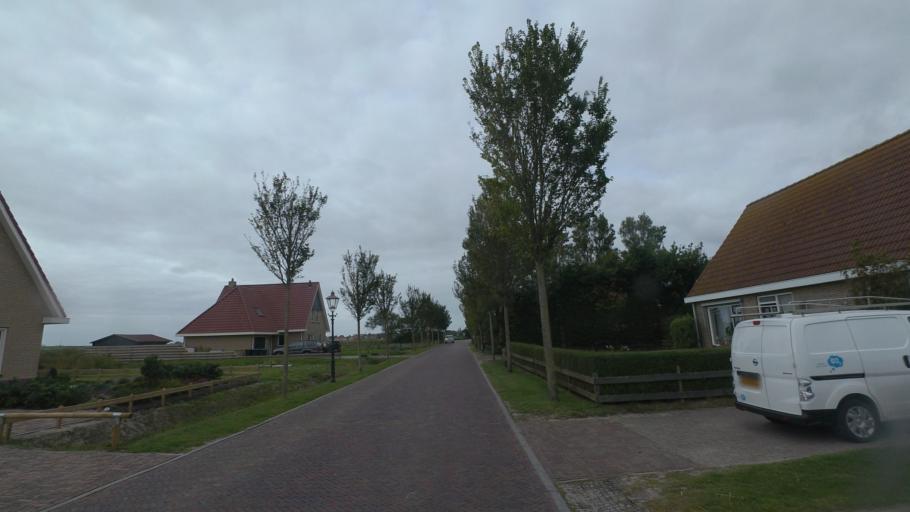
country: NL
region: Friesland
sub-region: Gemeente Ameland
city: Nes
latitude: 53.4464
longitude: 5.7937
